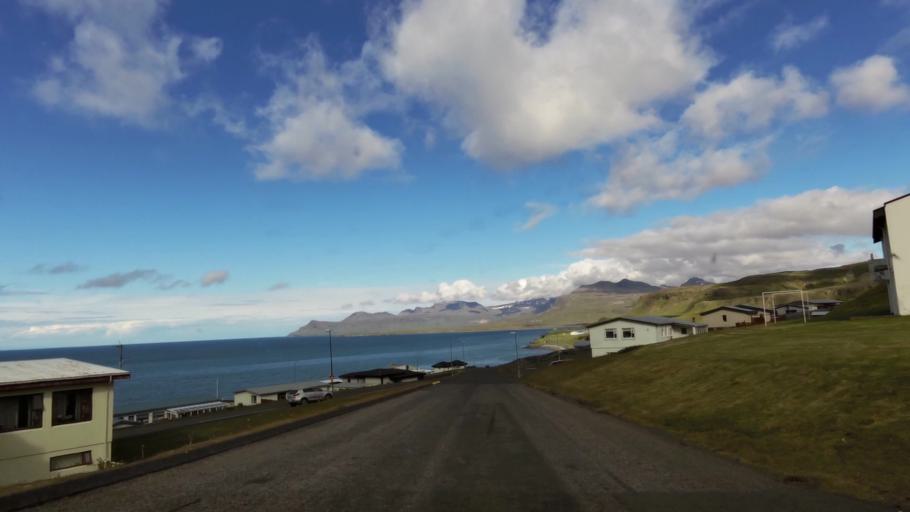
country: IS
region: West
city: Olafsvik
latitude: 64.8906
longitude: -23.7053
